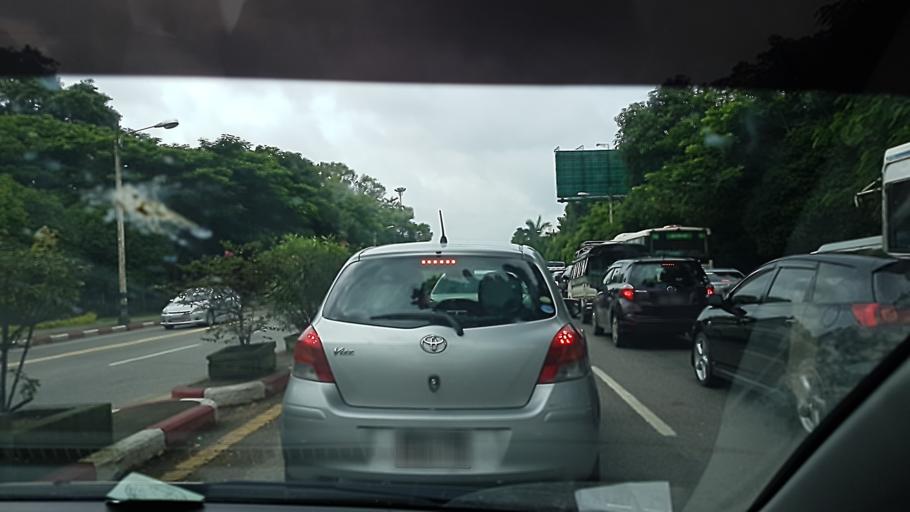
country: MM
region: Yangon
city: Yangon
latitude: 16.7944
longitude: 96.1399
